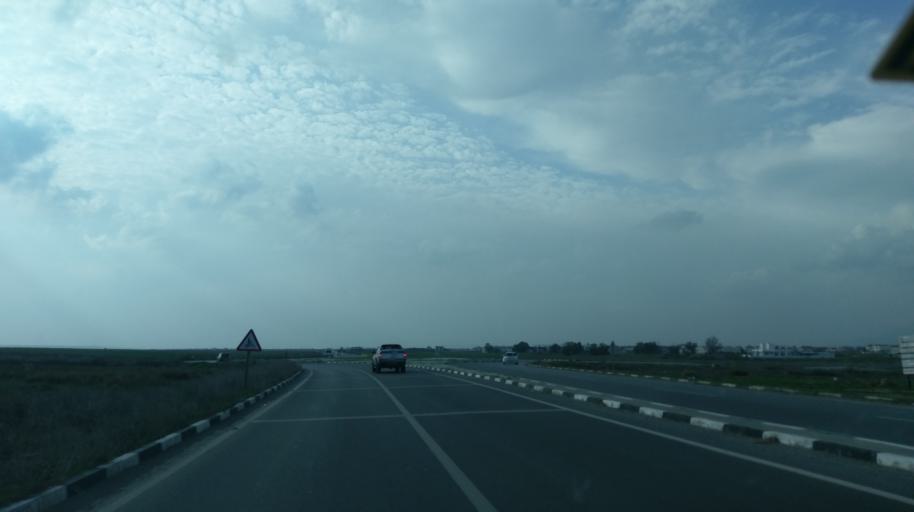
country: CY
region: Lefkosia
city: Nicosia
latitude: 35.1986
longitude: 33.3053
